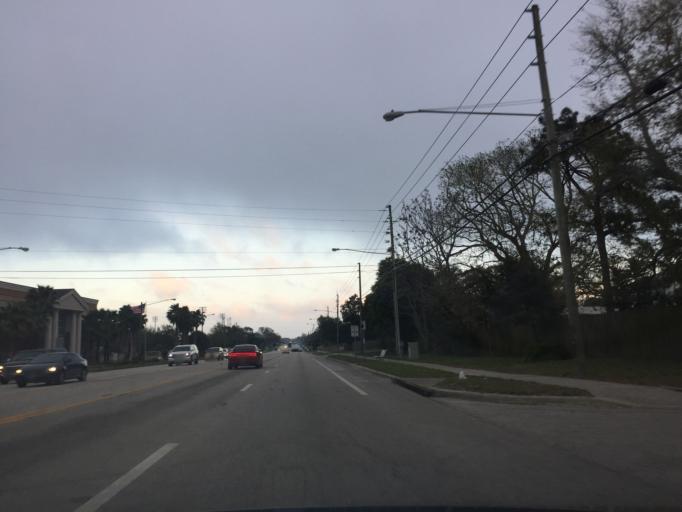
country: US
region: Florida
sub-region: Pinellas County
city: Safety Harbor
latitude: 27.9679
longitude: -82.7419
